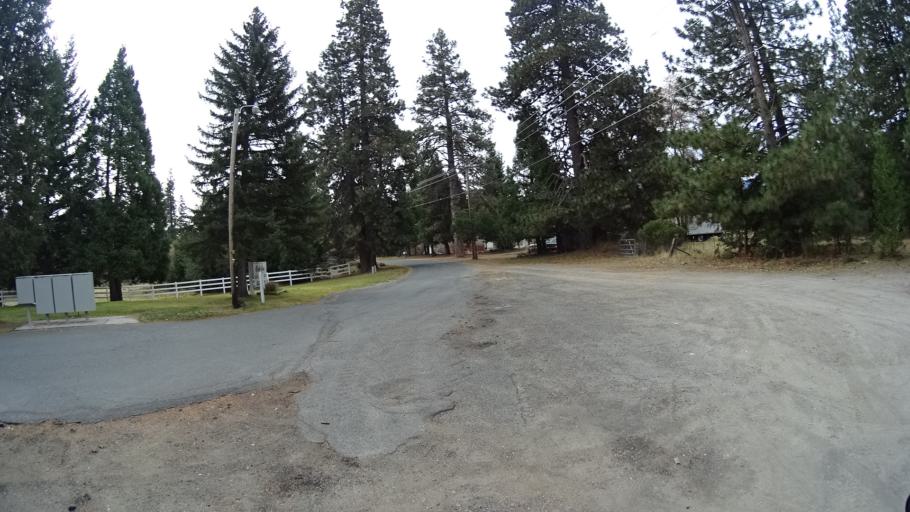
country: US
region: California
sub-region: Siskiyou County
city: Weed
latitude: 41.4032
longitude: -122.3808
